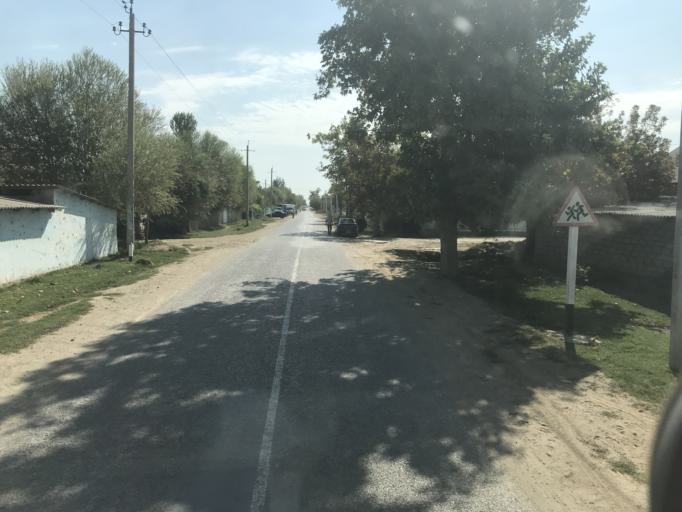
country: KZ
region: Ongtustik Qazaqstan
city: Myrzakent
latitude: 40.6643
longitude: 68.6177
